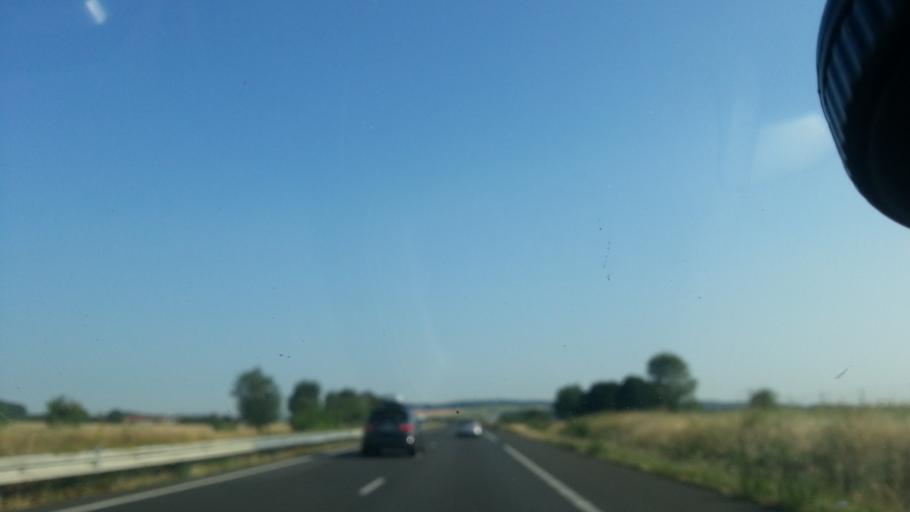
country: FR
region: Poitou-Charentes
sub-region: Departement de la Vienne
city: Antran
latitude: 46.8454
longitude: 0.5260
